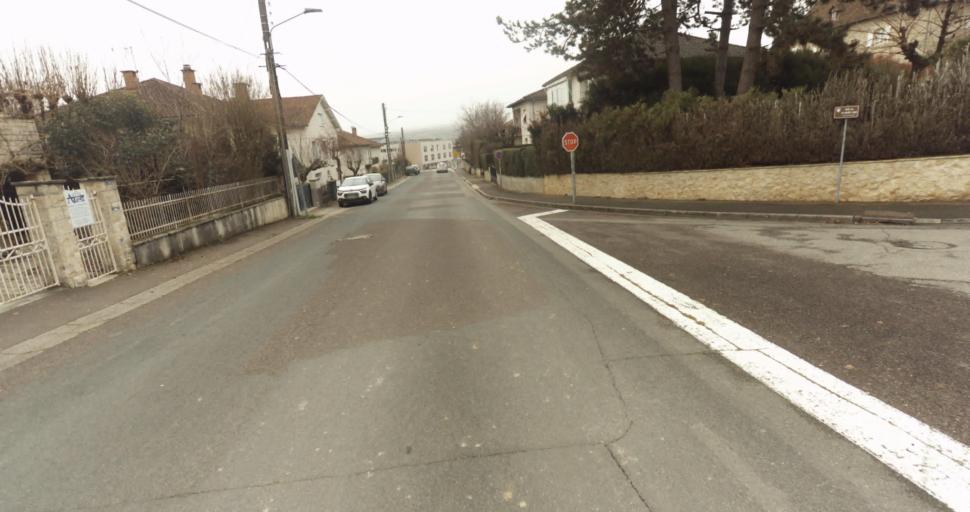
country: FR
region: Midi-Pyrenees
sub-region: Departement du Lot
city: Figeac
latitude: 44.6162
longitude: 2.0383
